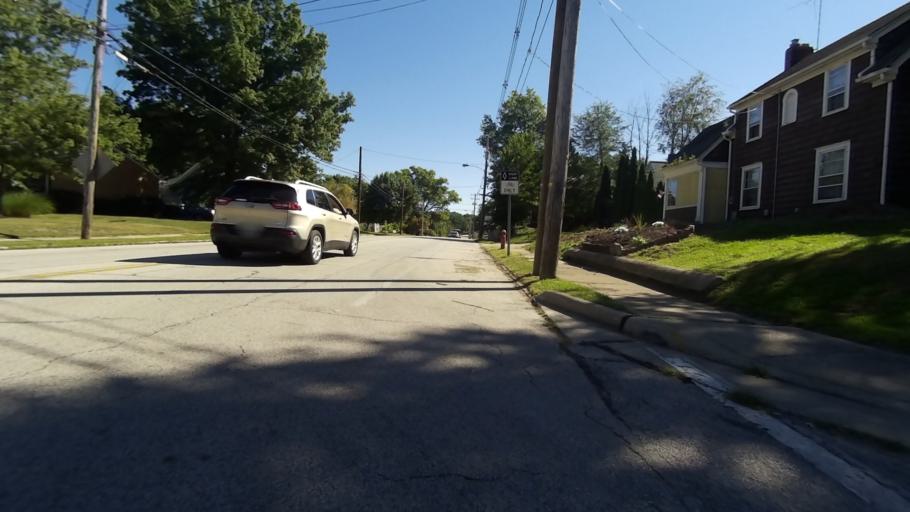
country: US
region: Ohio
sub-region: Portage County
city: Kent
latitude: 41.1518
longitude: -81.3765
